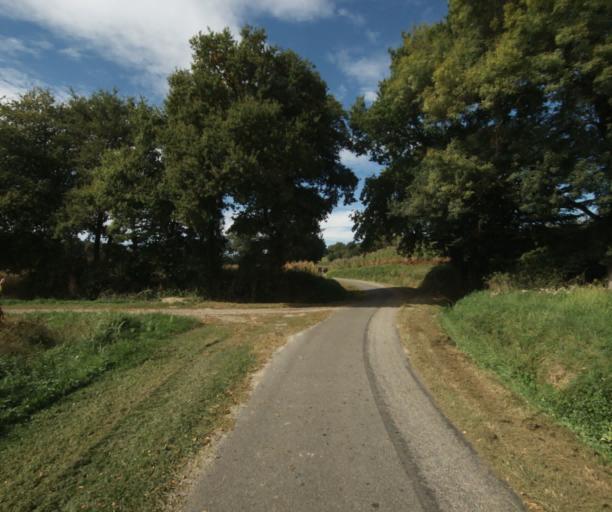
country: FR
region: Aquitaine
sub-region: Departement des Landes
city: Villeneuve-de-Marsan
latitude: 43.8980
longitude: -0.2100
